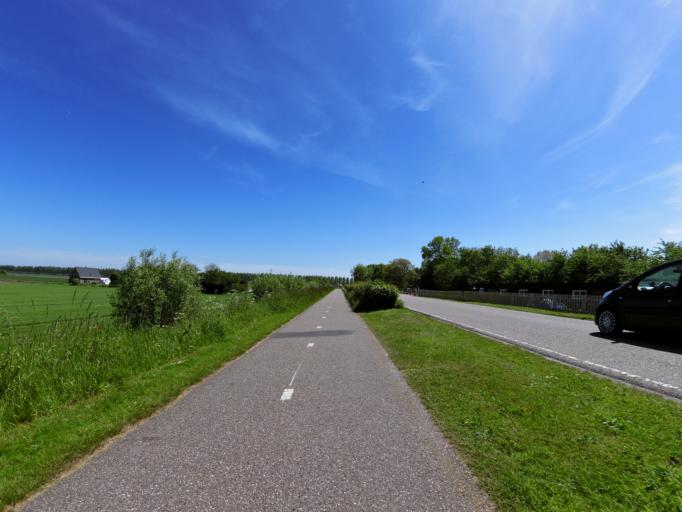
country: NL
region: South Holland
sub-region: Gemeente Hellevoetsluis
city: Nieuw-Helvoet
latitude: 51.8555
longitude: 4.0857
